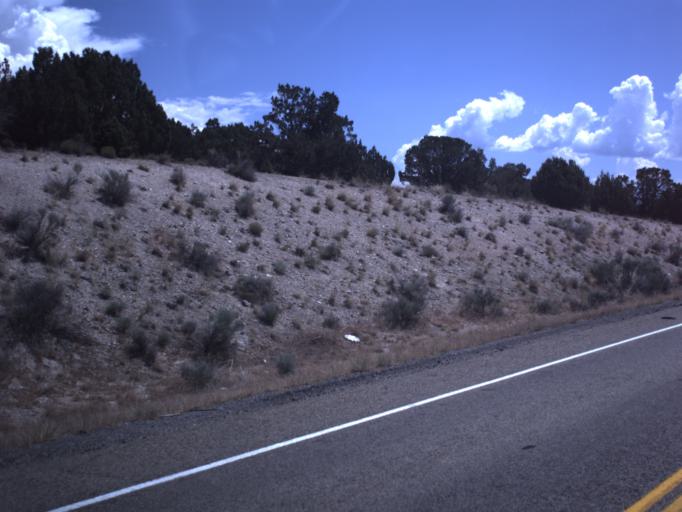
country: US
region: Utah
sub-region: Juab County
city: Nephi
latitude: 39.6666
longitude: -112.0494
